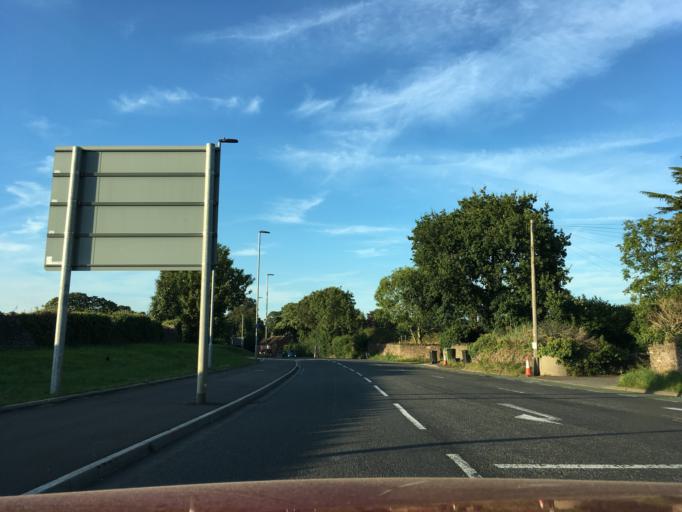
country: GB
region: England
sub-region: South Gloucestershire
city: Stoke Gifford
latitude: 51.5046
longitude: -2.5206
